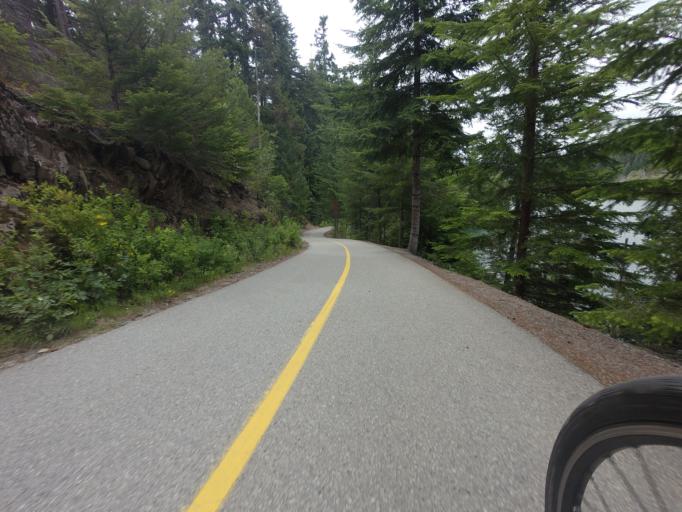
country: CA
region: British Columbia
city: Whistler
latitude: 50.1017
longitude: -122.9929
